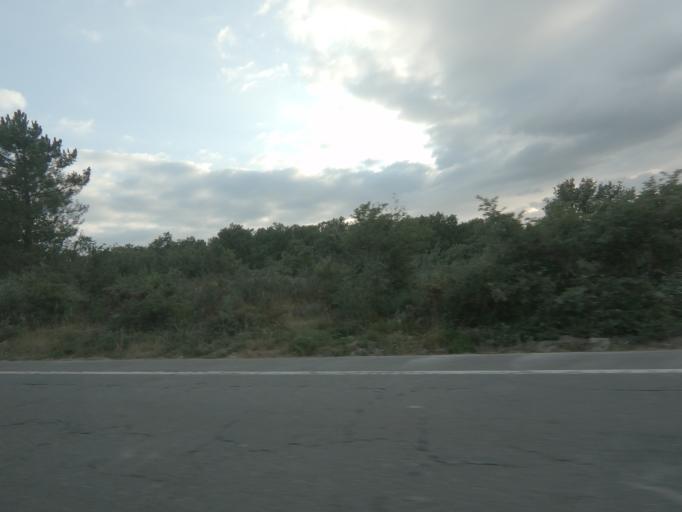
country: ES
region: Galicia
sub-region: Provincia de Ourense
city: Taboadela
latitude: 42.2766
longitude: -7.8363
